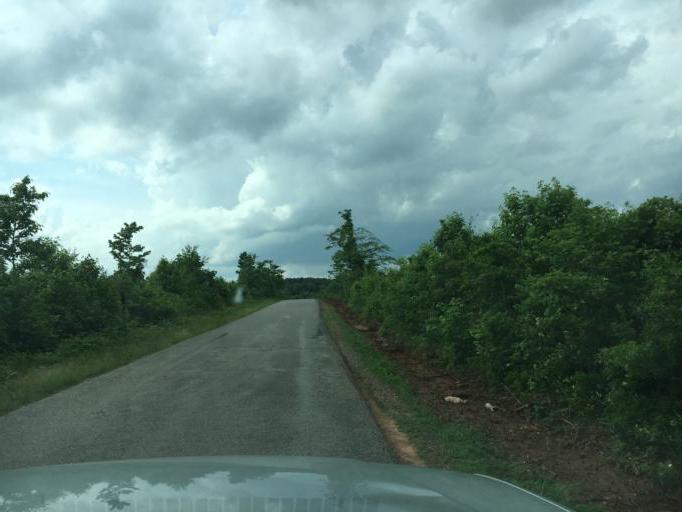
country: US
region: South Carolina
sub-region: Spartanburg County
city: Fairforest
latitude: 34.9207
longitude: -82.0475
